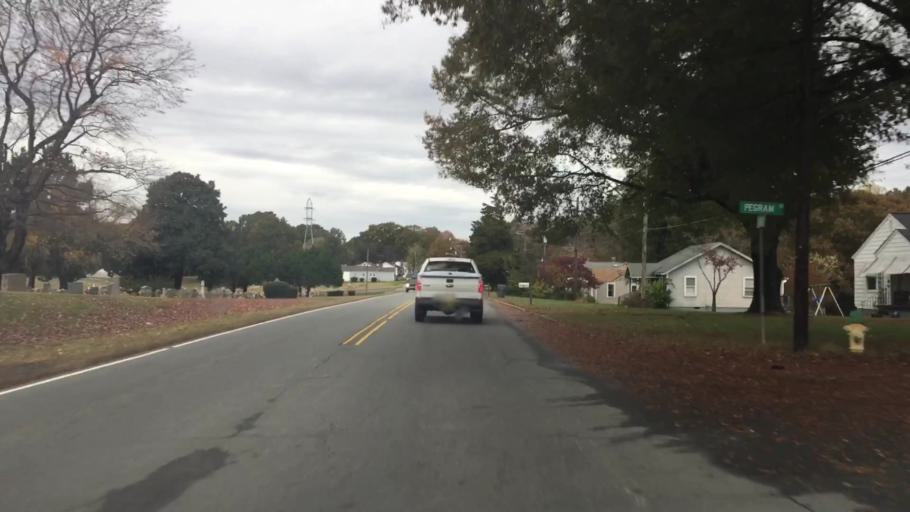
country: US
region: North Carolina
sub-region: Rockingham County
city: Reidsville
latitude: 36.3407
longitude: -79.6534
